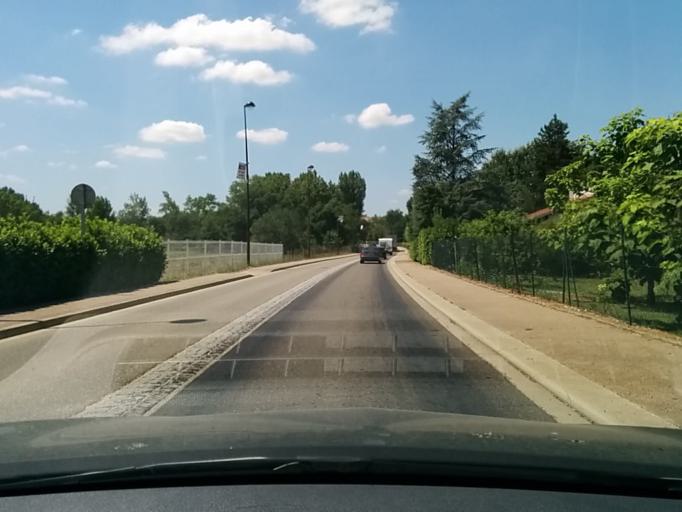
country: FR
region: Midi-Pyrenees
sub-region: Departement du Gers
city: Vic-Fezensac
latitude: 43.7549
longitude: 0.3073
